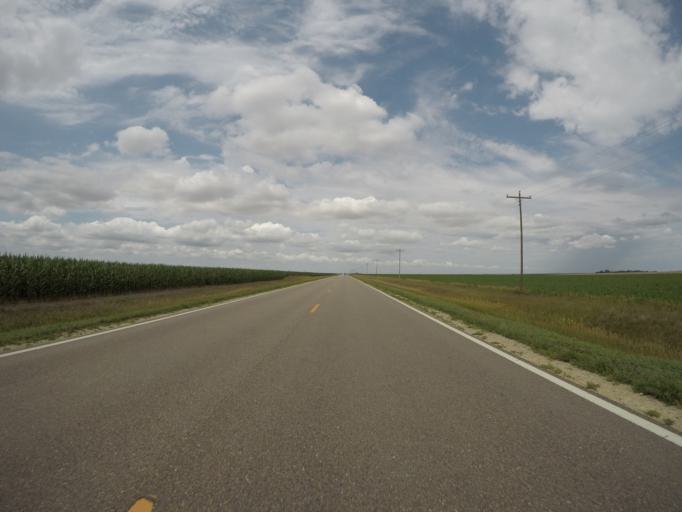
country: US
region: Kansas
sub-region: Rawlins County
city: Atwood
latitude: 39.6576
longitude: -101.0569
